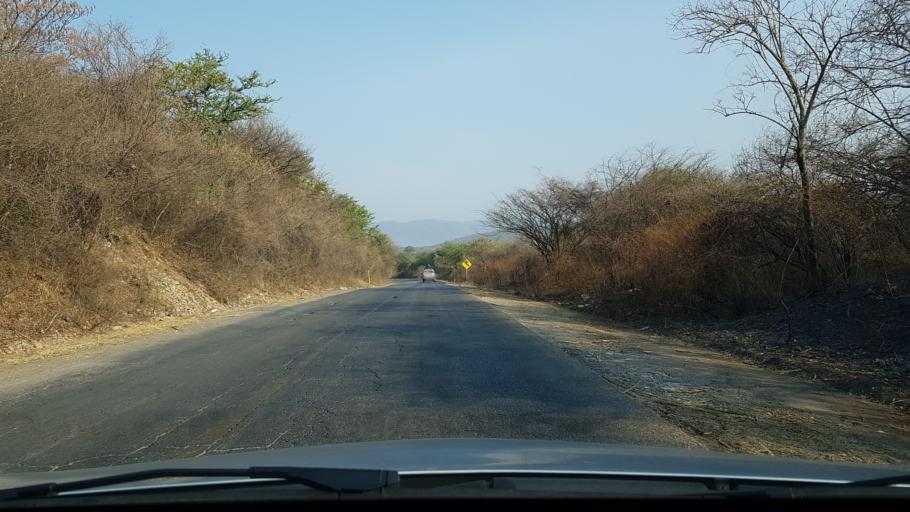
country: MX
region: Morelos
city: Tlaltizapan
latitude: 18.6784
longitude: -99.0869
